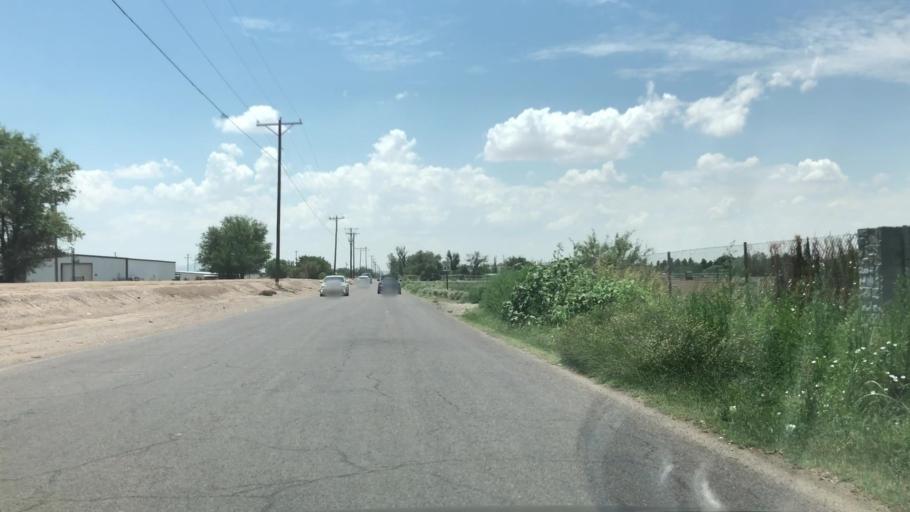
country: US
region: Texas
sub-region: El Paso County
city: Canutillo
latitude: 31.9183
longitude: -106.6247
